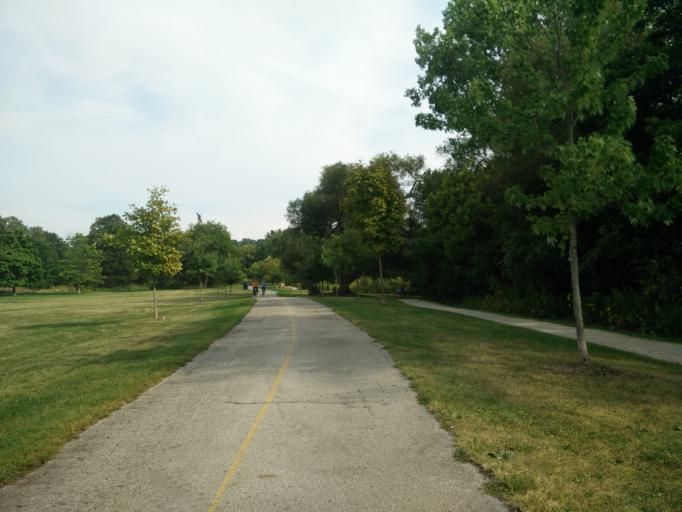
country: CA
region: Ontario
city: Etobicoke
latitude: 43.6607
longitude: -79.5016
